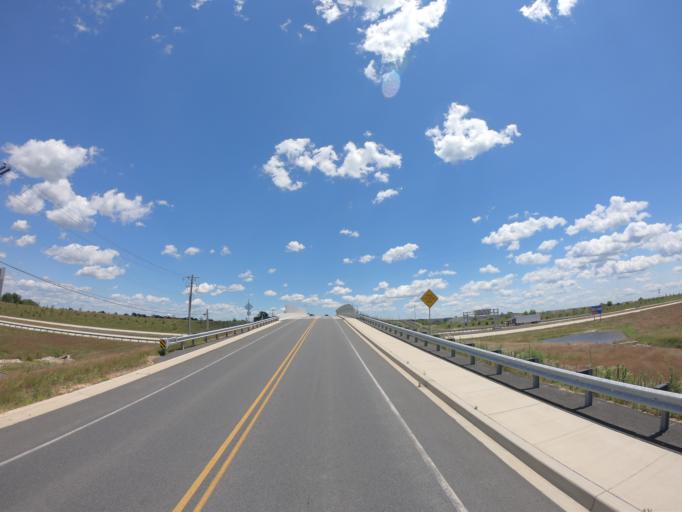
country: US
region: Delaware
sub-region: New Castle County
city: Middletown
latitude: 39.4569
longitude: -75.7423
